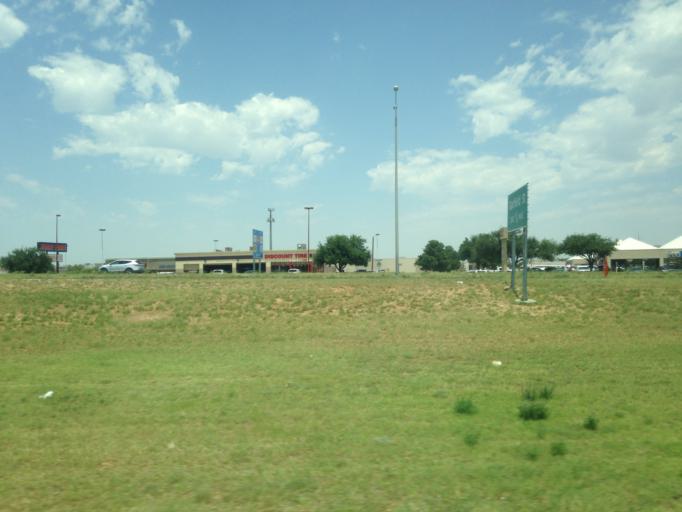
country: US
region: Texas
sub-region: Midland County
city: Midland
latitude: 32.0339
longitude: -102.1262
